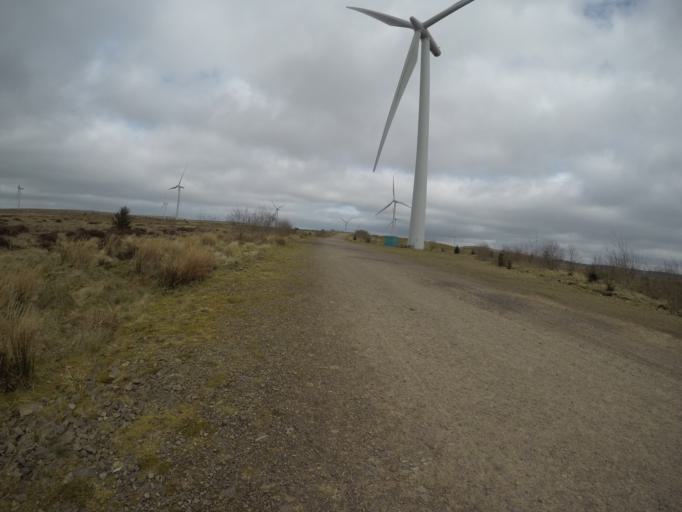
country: GB
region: Scotland
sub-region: East Renfrewshire
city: Newton Mearns
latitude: 55.7000
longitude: -4.3416
